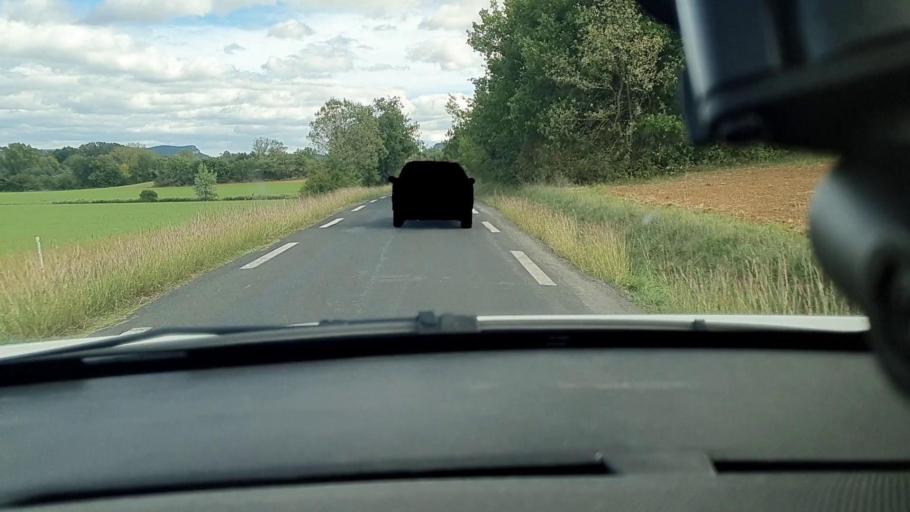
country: FR
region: Languedoc-Roussillon
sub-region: Departement du Gard
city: Les Mages
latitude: 44.2010
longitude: 4.2072
